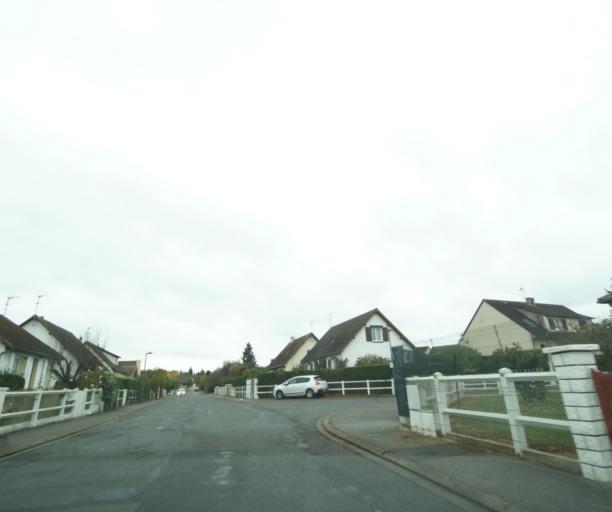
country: FR
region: Centre
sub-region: Departement d'Eure-et-Loir
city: Vernouillet
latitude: 48.7207
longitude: 1.3783
